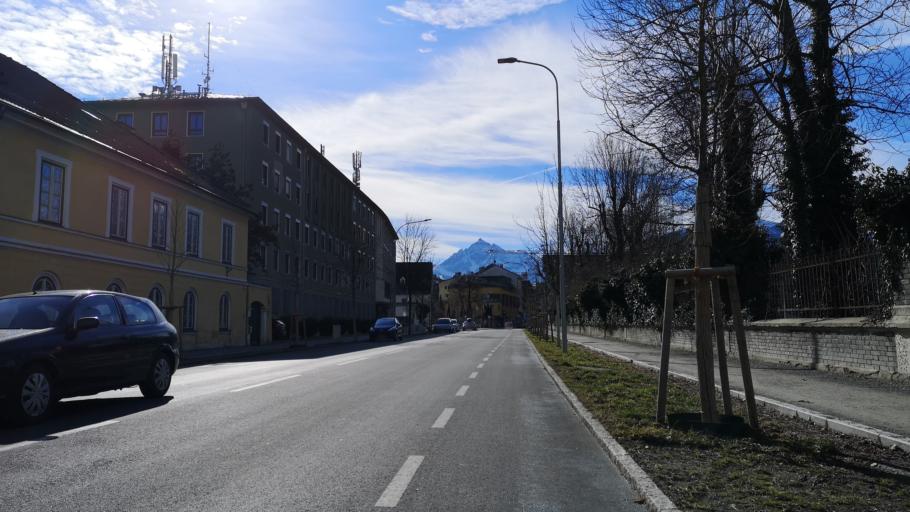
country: AT
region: Tyrol
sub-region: Innsbruck Stadt
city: Innsbruck
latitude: 47.2715
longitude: 11.4001
